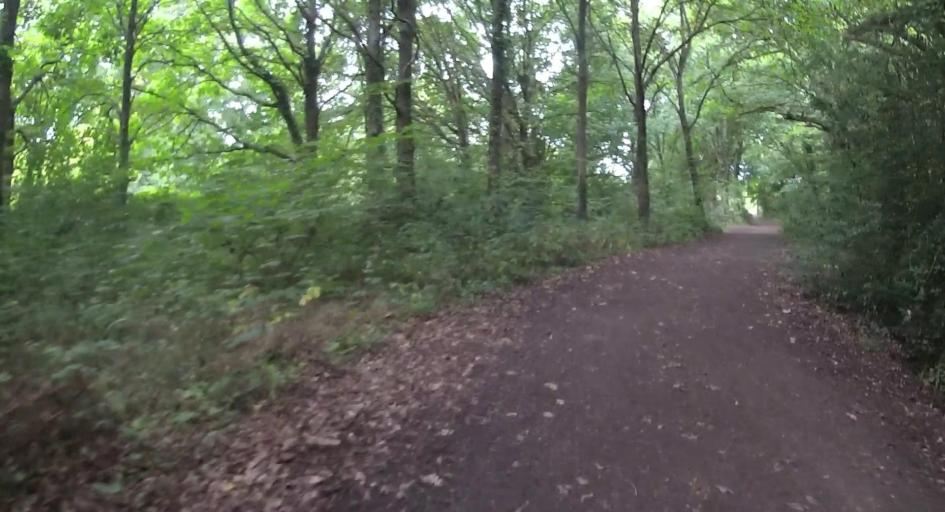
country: GB
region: England
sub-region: Surrey
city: Woking
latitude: 51.3424
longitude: -0.5624
